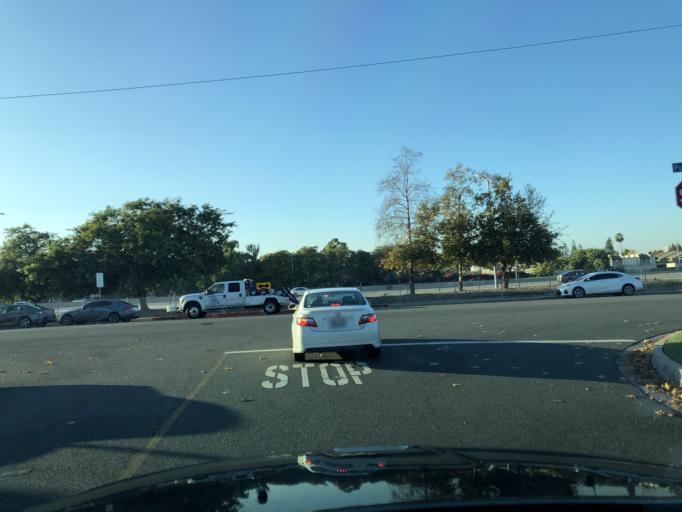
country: US
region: California
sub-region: Orange County
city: Costa Mesa
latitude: 33.6764
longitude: -117.8812
